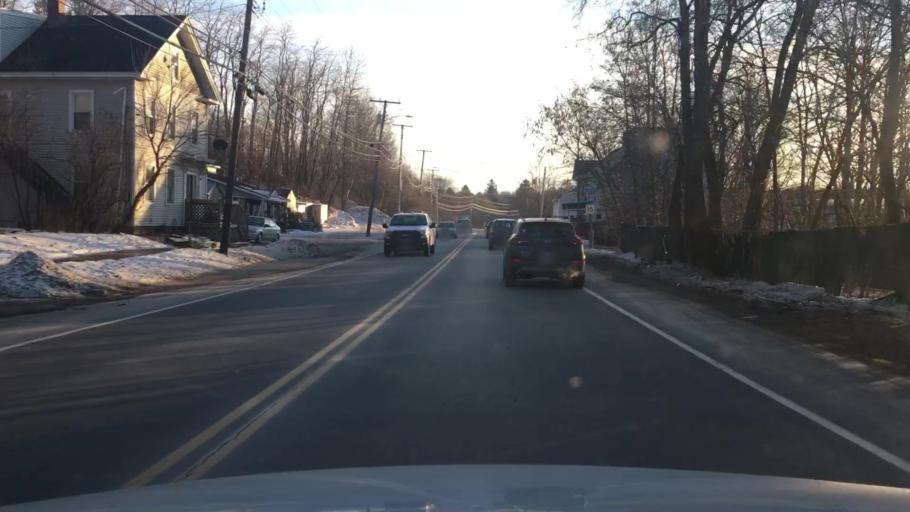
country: US
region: Maine
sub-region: Penobscot County
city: Brewer
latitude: 44.7880
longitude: -68.7706
